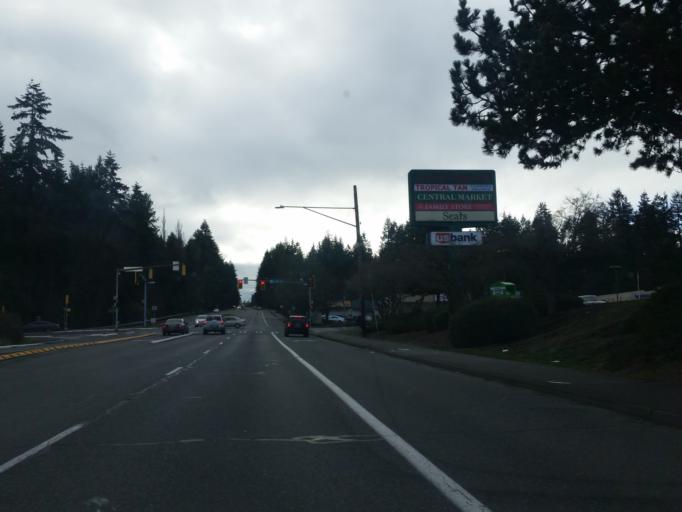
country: US
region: Washington
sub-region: King County
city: Shoreline
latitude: 47.7423
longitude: -122.3471
